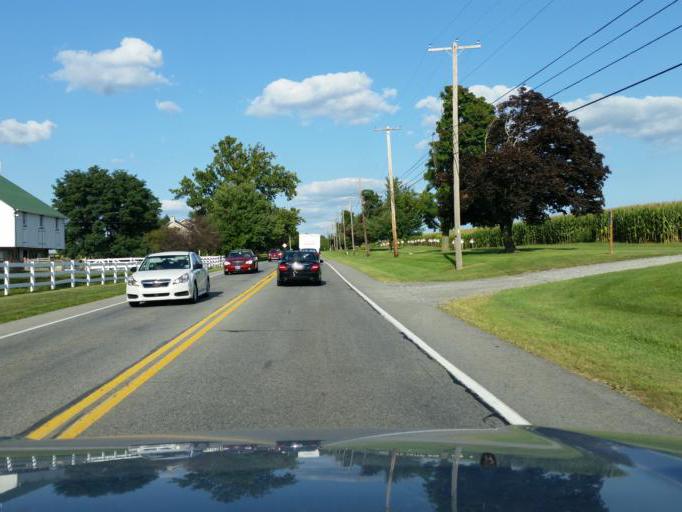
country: US
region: Pennsylvania
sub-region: Dauphin County
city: Palmdale
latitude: 40.2759
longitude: -76.6163
